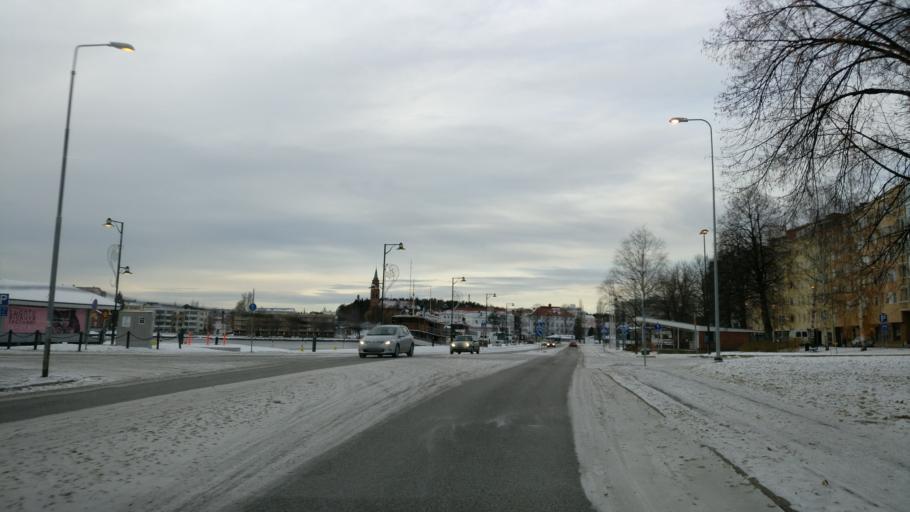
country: FI
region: Southern Savonia
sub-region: Savonlinna
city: Savonlinna
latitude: 61.8663
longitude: 28.8884
